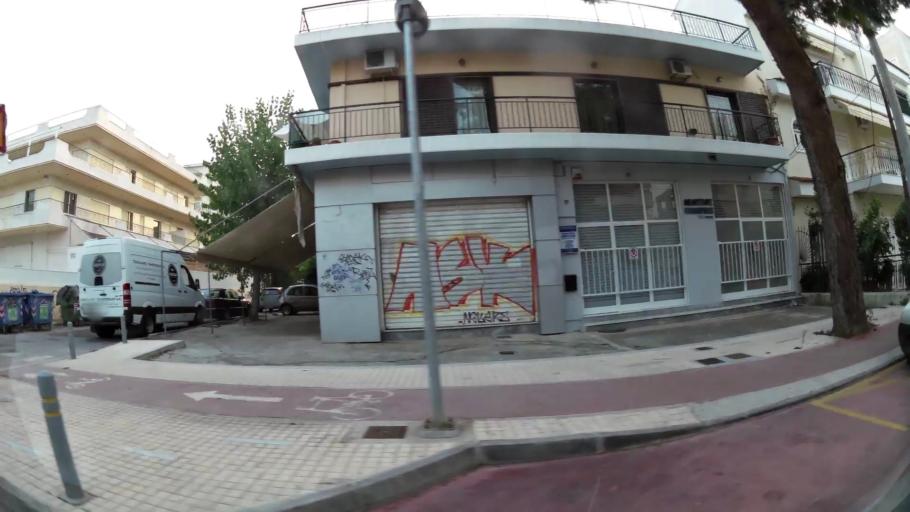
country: GR
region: Attica
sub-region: Nomarchia Athinas
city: Agia Paraskevi
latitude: 38.0182
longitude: 23.8312
